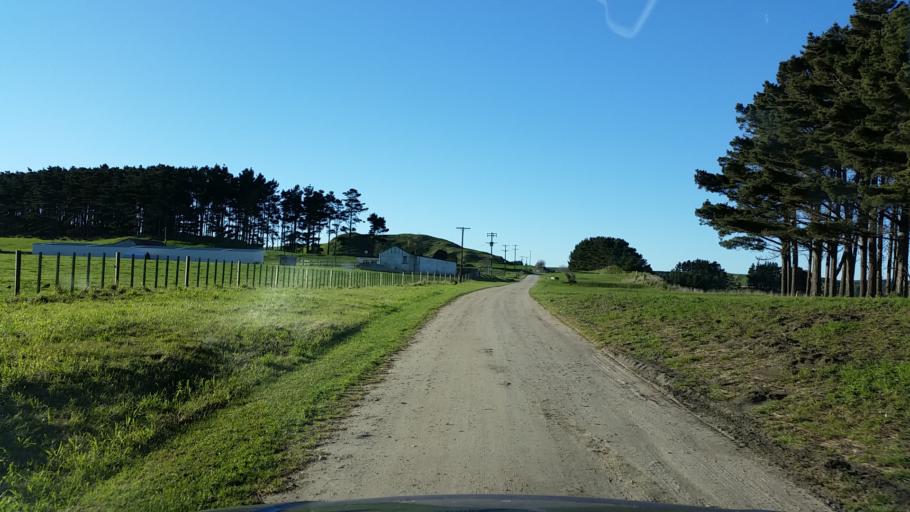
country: NZ
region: Taranaki
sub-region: South Taranaki District
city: Patea
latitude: -39.8375
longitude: 174.7050
